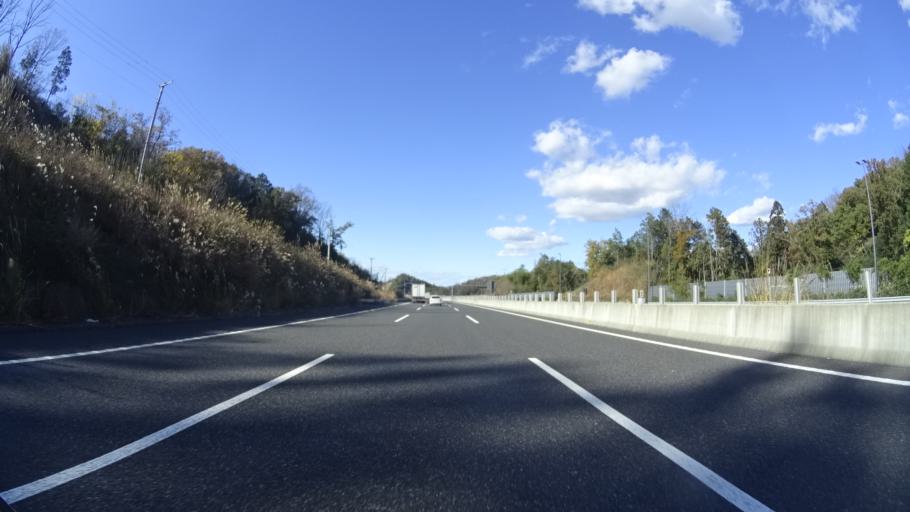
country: JP
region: Aichi
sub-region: Toyota-shi
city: Toyota
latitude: 35.0348
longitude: 137.2183
